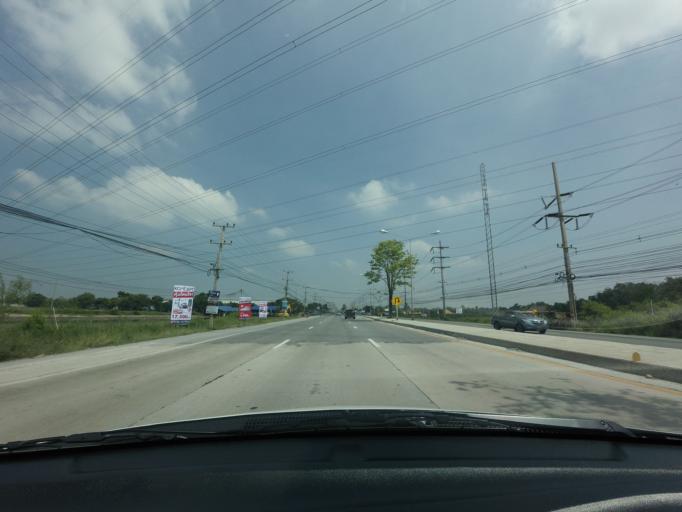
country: TH
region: Chachoengsao
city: Bang Pakong
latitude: 13.5661
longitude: 100.9985
